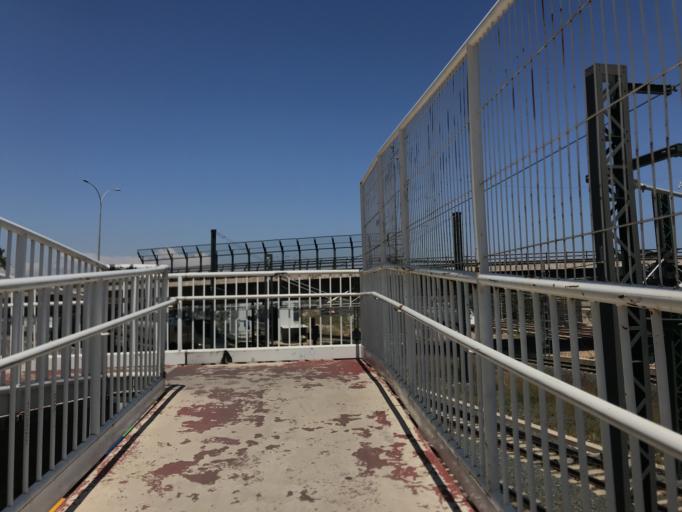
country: ES
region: Valencia
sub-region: Provincia de Valencia
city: Valencia
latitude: 39.4547
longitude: -0.3815
